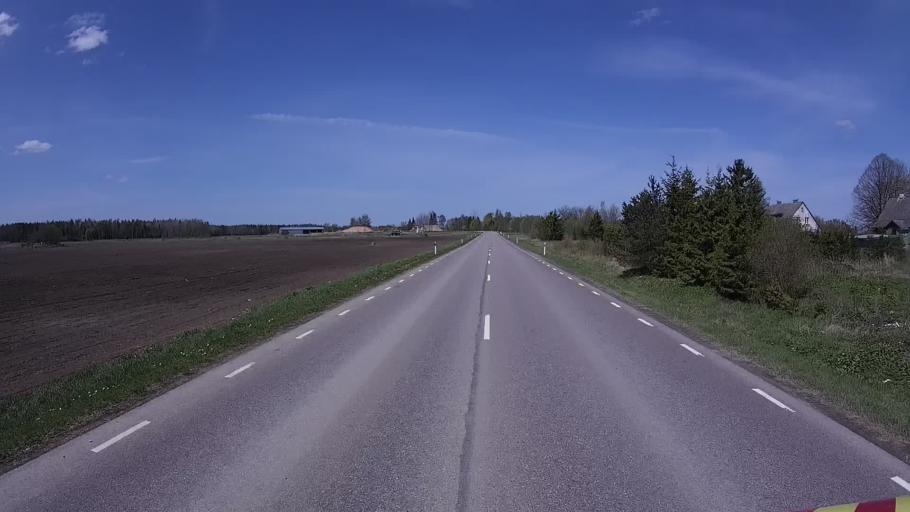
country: EE
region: Harju
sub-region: Keila linn
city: Keila
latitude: 59.3064
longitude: 24.3233
